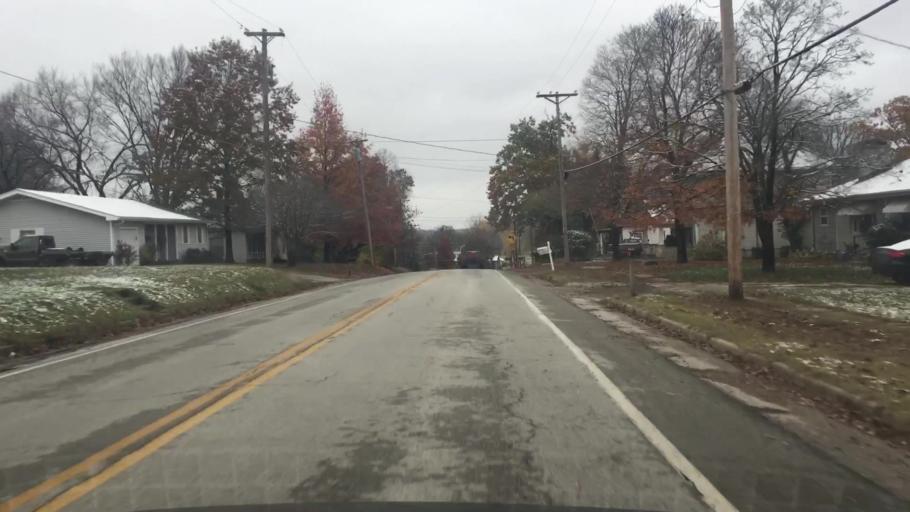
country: US
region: Missouri
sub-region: Saint Clair County
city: Osceola
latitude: 38.0405
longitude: -93.7025
